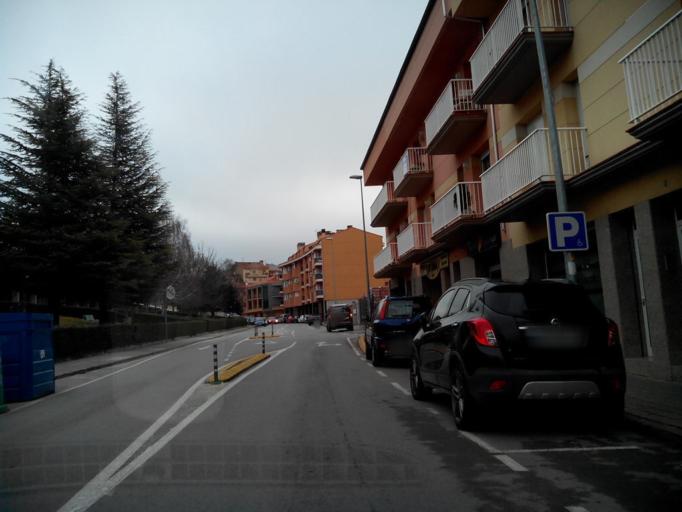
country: ES
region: Catalonia
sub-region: Provincia de Barcelona
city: Berga
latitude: 42.1032
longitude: 1.8531
